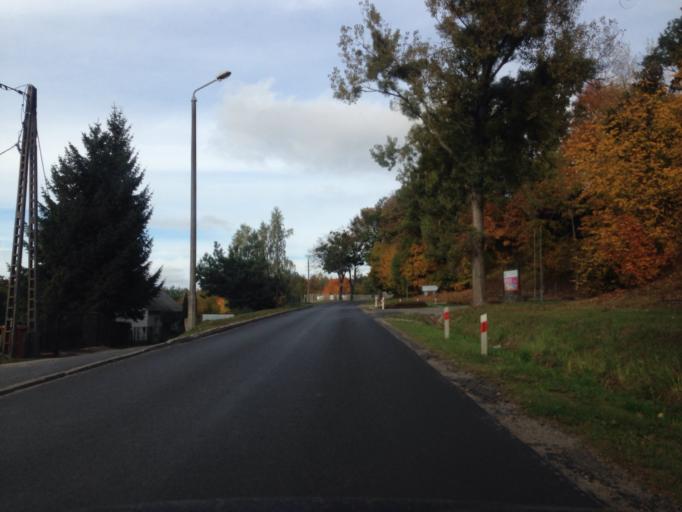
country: PL
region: Kujawsko-Pomorskie
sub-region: Powiat brodnicki
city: Brodnica
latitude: 53.2760
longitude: 19.3883
